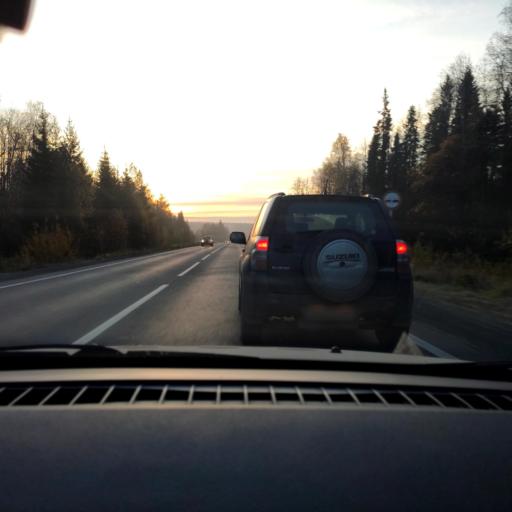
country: RU
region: Perm
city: Novyye Lyady
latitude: 58.0423
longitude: 56.4492
